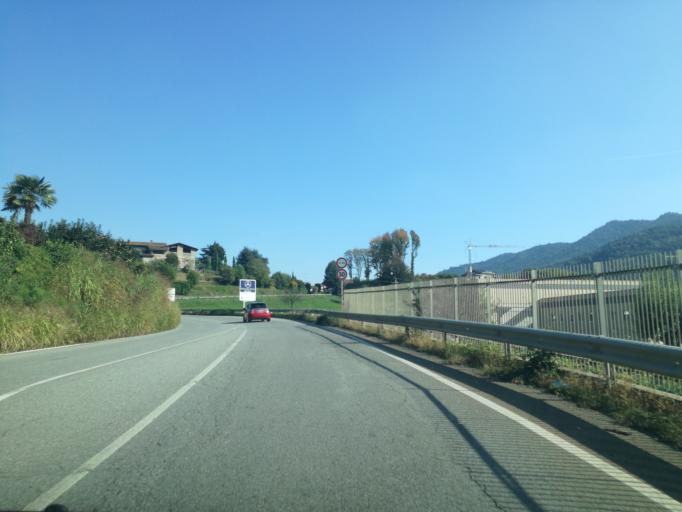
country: IT
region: Lombardy
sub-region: Provincia di Bergamo
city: Cisano Bergamasco
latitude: 45.7410
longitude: 9.4625
